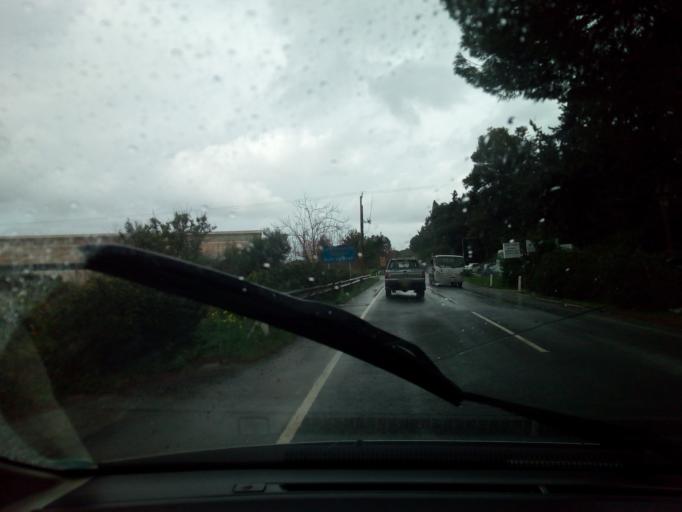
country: CY
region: Pafos
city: Polis
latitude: 35.0217
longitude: 32.4334
